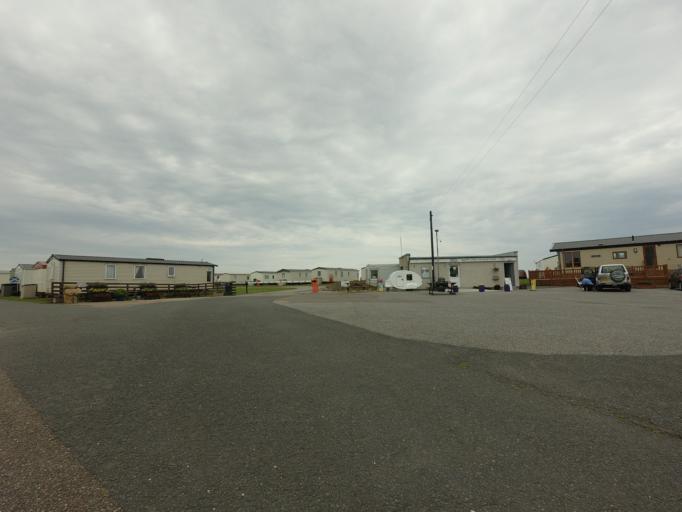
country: GB
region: Scotland
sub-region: Aberdeenshire
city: Banff
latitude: 57.6700
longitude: -2.5533
